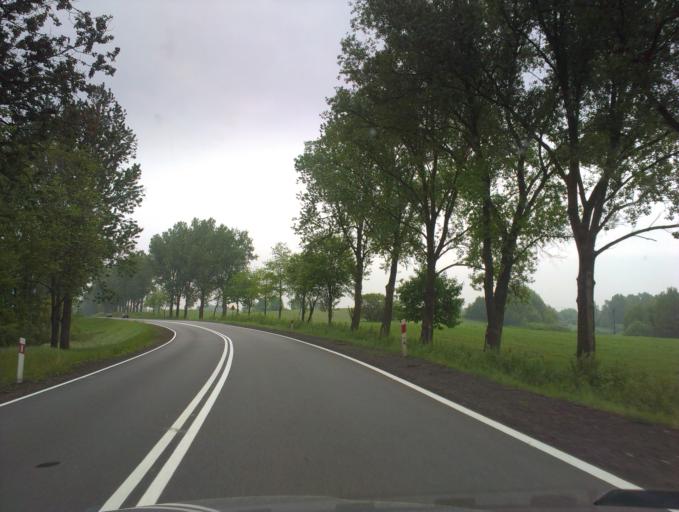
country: PL
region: West Pomeranian Voivodeship
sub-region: Powiat koszalinski
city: Bobolice
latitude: 53.9322
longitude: 16.5977
